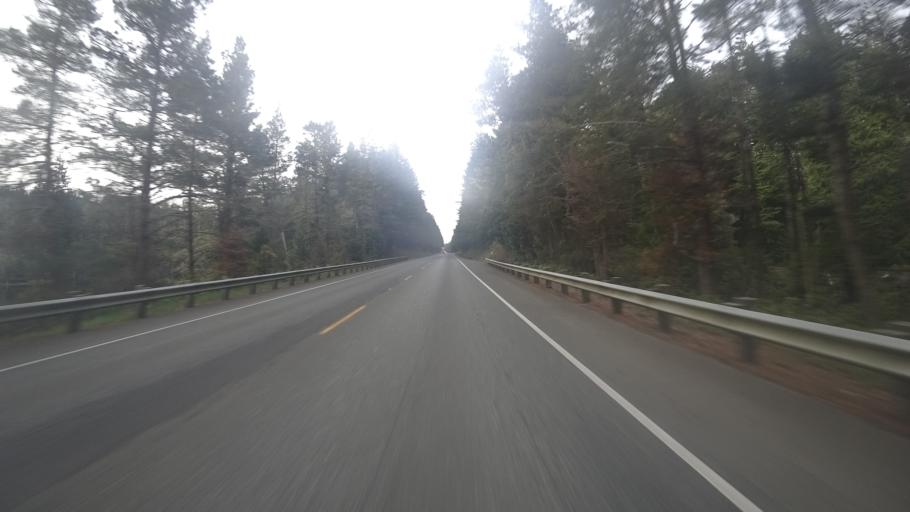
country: US
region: Oregon
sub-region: Coos County
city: Lakeside
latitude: 43.5431
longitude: -124.2129
